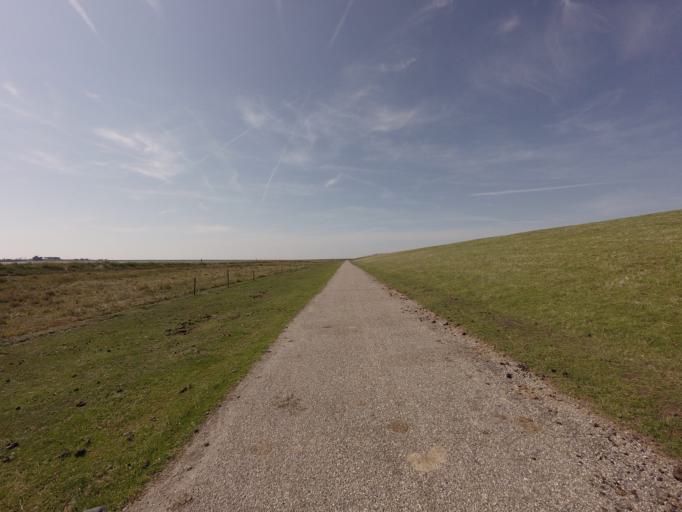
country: NL
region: Friesland
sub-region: Gemeente Schiermonnikoog
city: Schiermonnikoog
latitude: 53.4748
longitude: 6.2060
